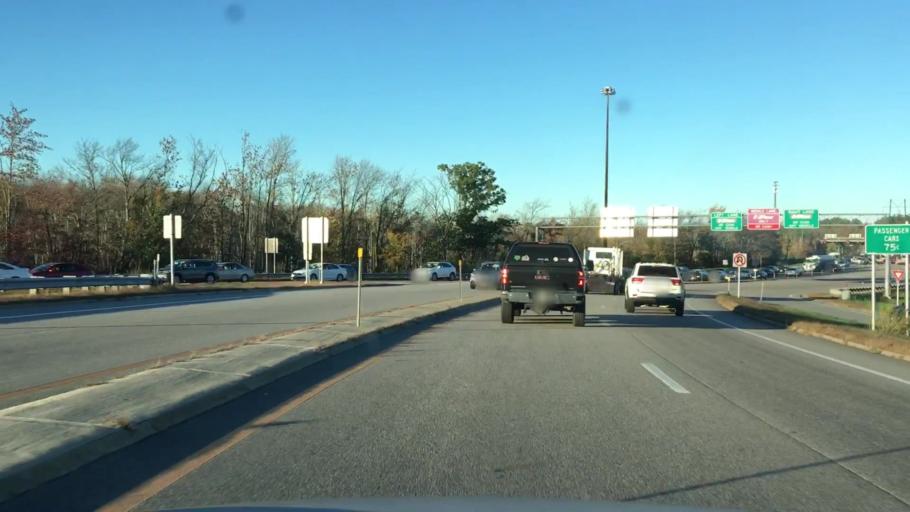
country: US
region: New Hampshire
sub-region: Rockingham County
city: North Hampton
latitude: 42.9627
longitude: -70.8631
